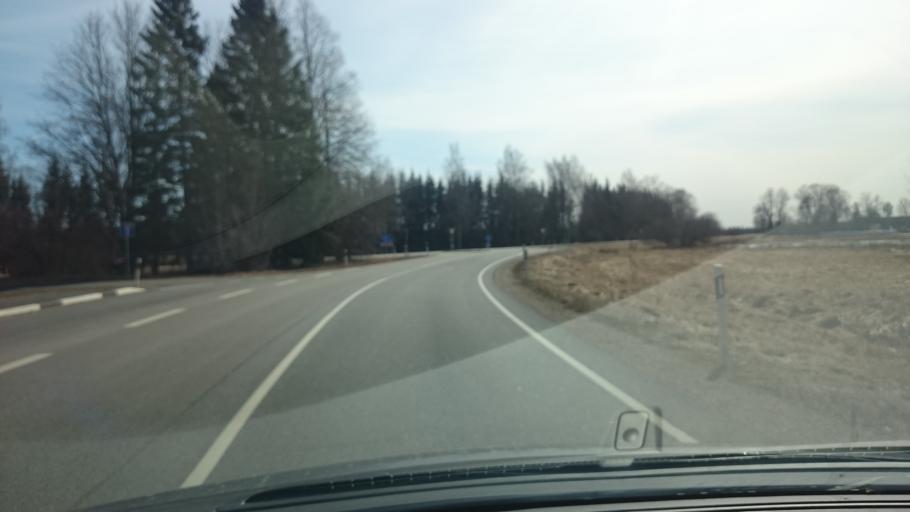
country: EE
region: Paernumaa
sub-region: Vaendra vald (alev)
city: Vandra
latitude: 58.6270
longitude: 24.9232
